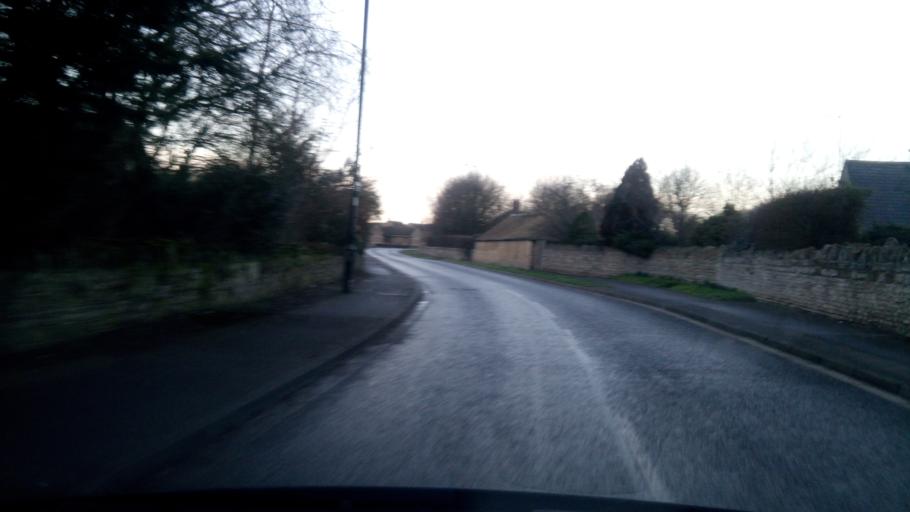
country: GB
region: England
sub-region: Peterborough
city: Castor
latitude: 52.5735
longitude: -0.3478
